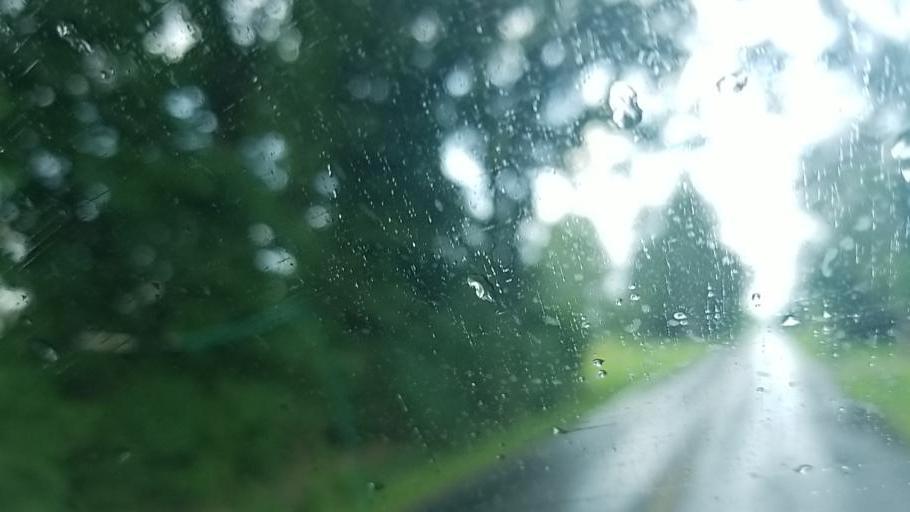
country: US
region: Ohio
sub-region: Lorain County
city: Lagrange
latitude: 41.1838
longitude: -82.0534
